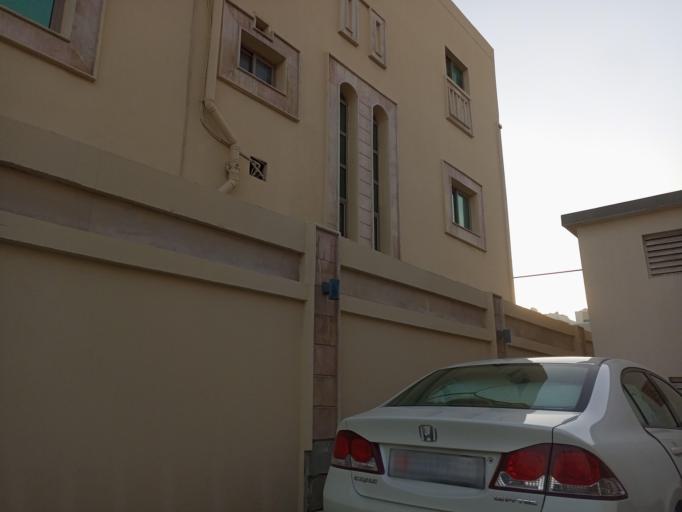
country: BH
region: Muharraq
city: Al Hadd
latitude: 26.2311
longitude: 50.6484
